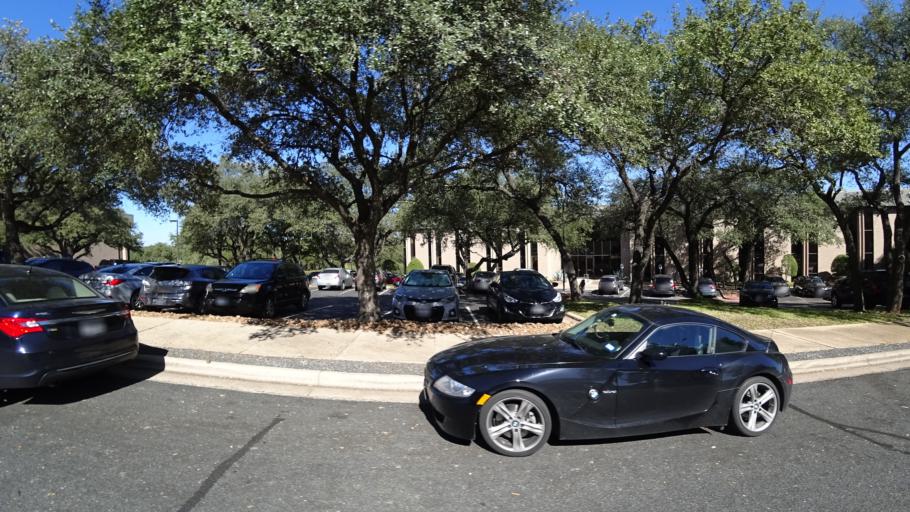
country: US
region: Texas
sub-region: Travis County
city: West Lake Hills
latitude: 30.3621
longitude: -97.7491
